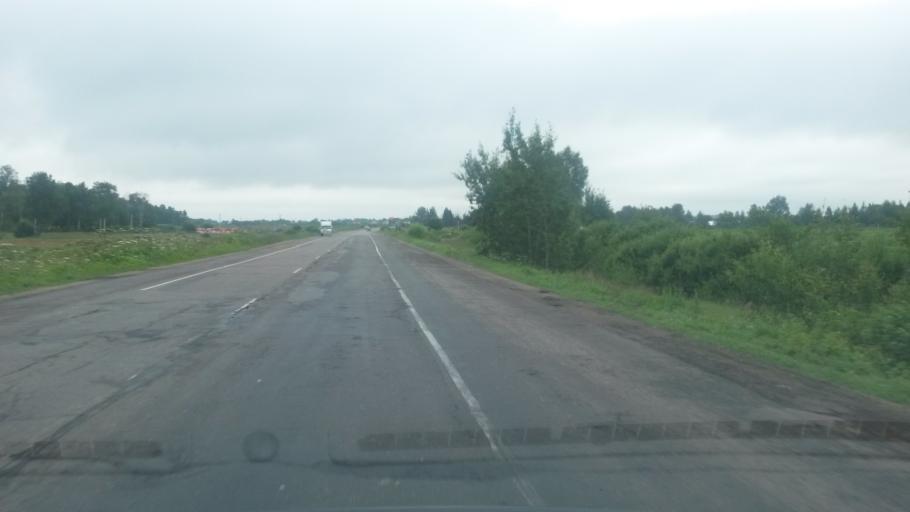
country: RU
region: Ivanovo
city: Novo-Talitsy
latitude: 57.0133
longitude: 40.8192
